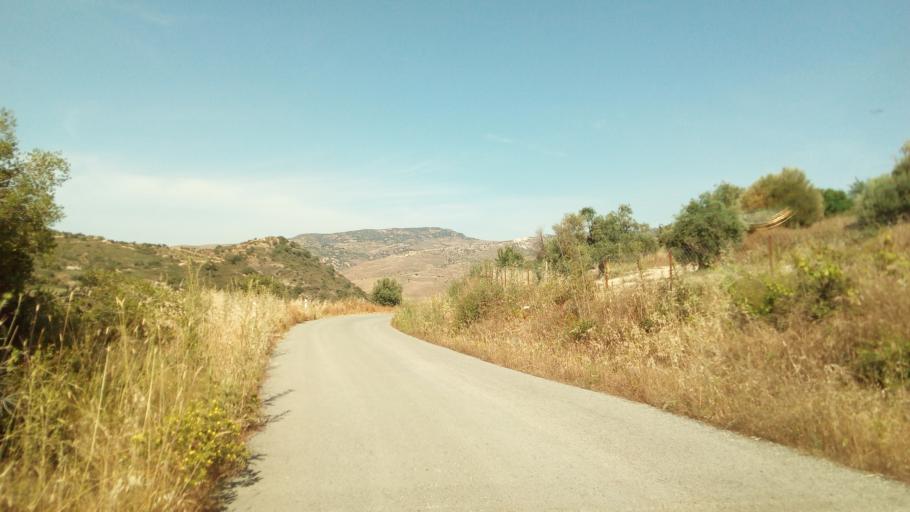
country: CY
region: Limassol
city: Pachna
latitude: 34.8150
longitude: 32.7346
